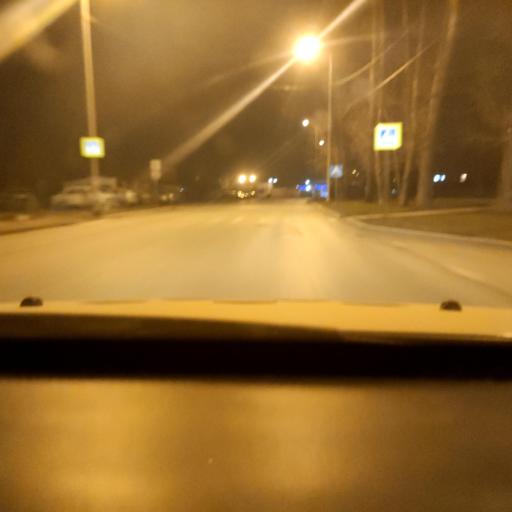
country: RU
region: Perm
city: Kondratovo
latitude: 57.9599
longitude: 56.1714
